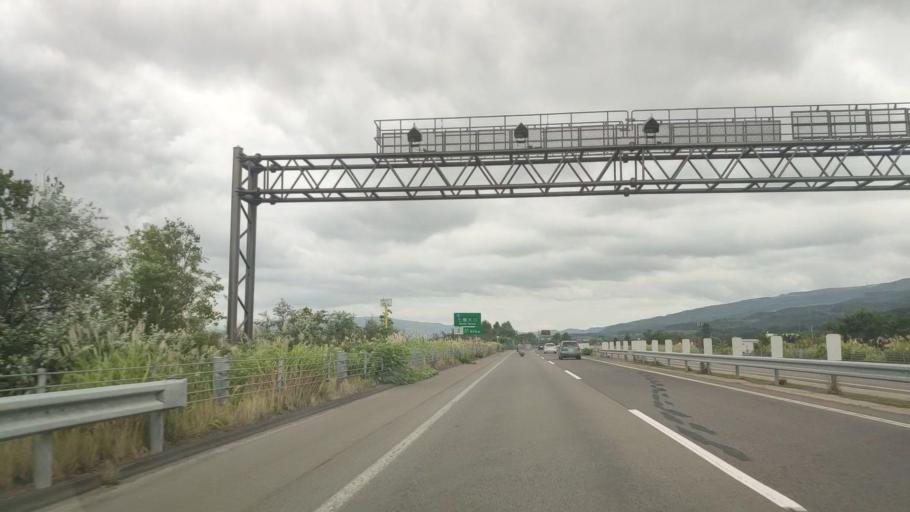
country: JP
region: Hokkaido
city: Nanae
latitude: 41.8609
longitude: 140.7332
